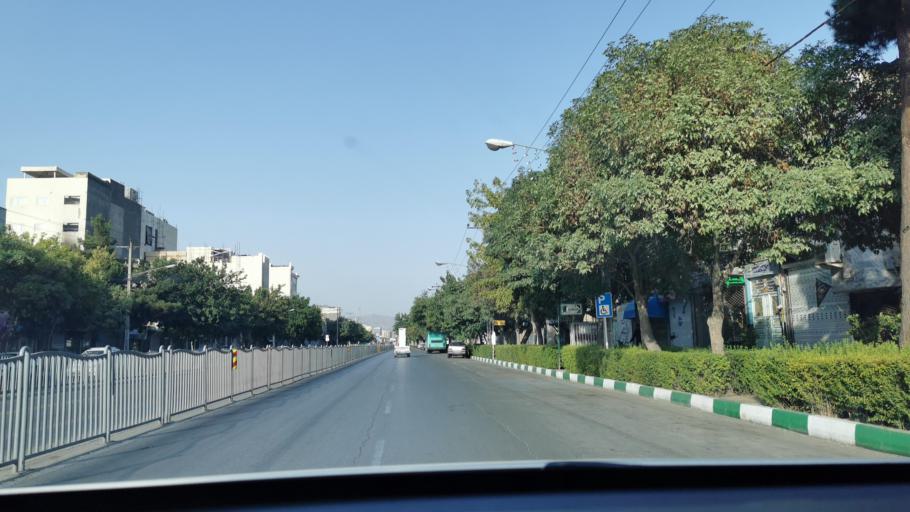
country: IR
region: Razavi Khorasan
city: Mashhad
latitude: 36.3044
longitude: 59.6417
